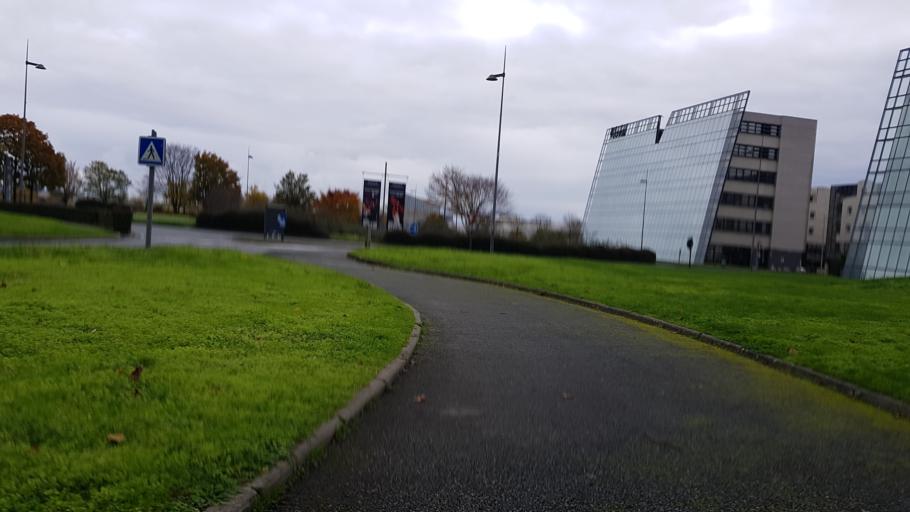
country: FR
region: Poitou-Charentes
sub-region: Departement de la Vienne
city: Chasseneuil-du-Poitou
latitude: 46.6636
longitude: 0.3605
